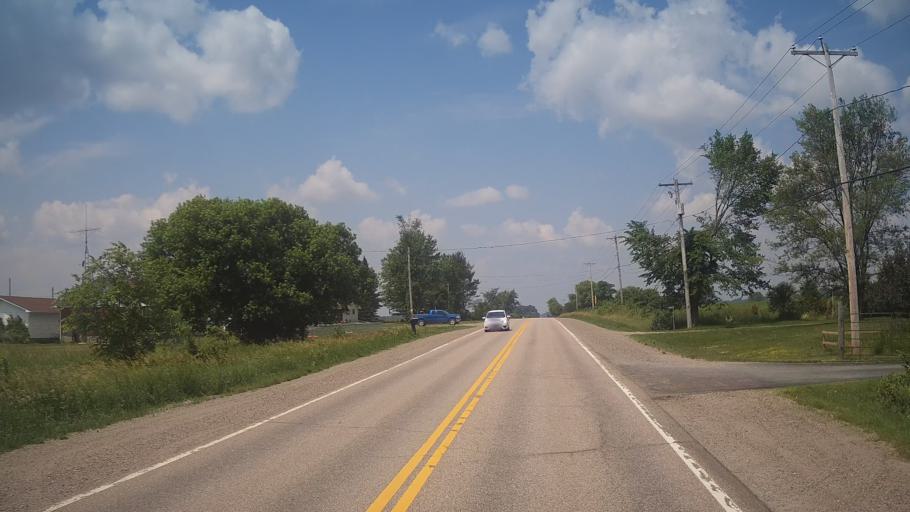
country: CA
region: Quebec
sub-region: Outaouais
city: Shawville
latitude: 45.5872
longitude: -76.4603
